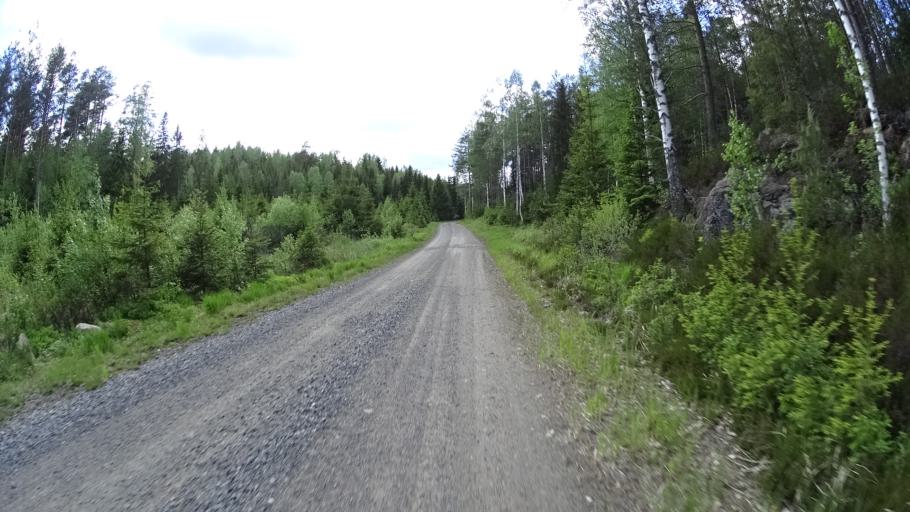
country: FI
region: Varsinais-Suomi
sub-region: Salo
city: Kisko
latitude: 60.1790
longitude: 23.5188
